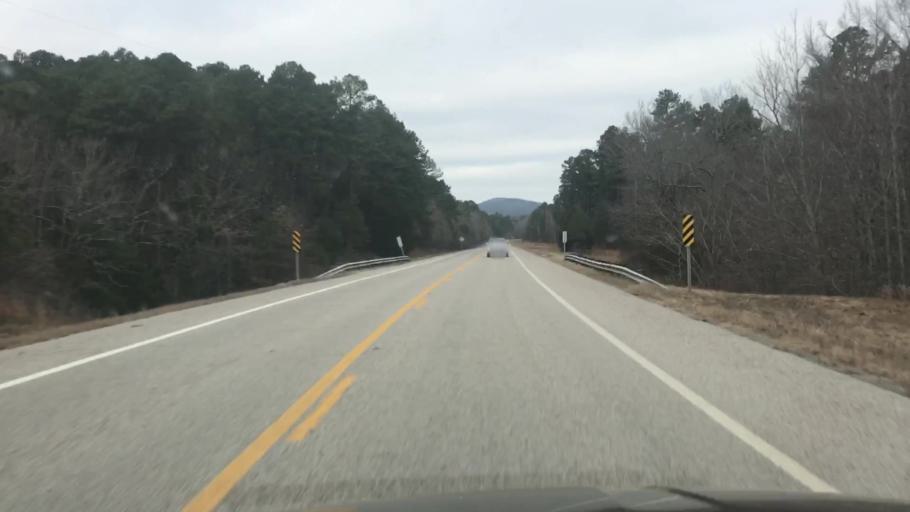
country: US
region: Arkansas
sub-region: Scott County
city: Waldron
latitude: 34.7112
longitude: -93.9402
